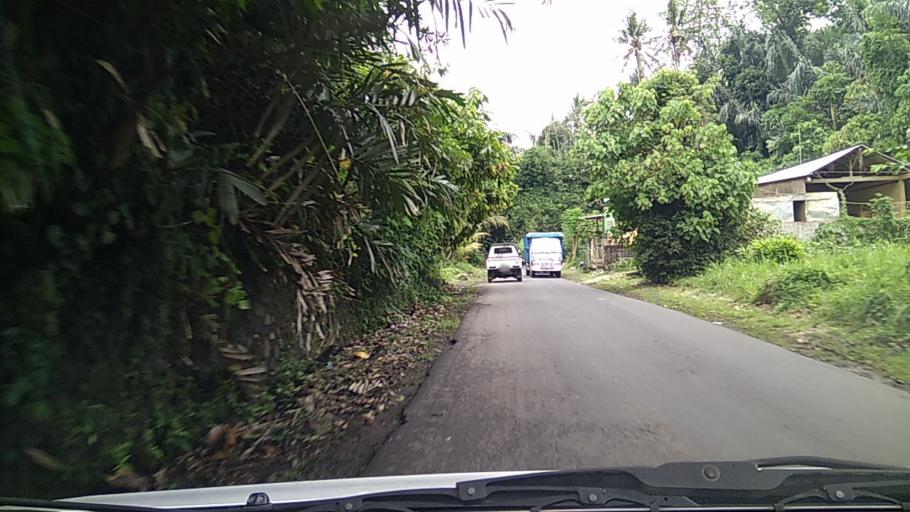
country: ID
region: Bali
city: Banjar Keraman
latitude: -8.5222
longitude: 115.2147
